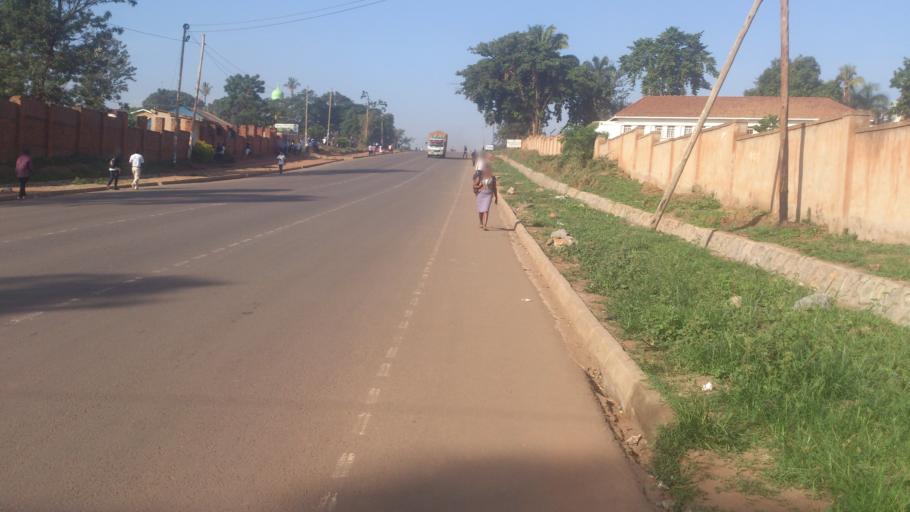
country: UG
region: Eastern Region
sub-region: Mbale District
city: Mbale
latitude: 1.0796
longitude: 34.1744
